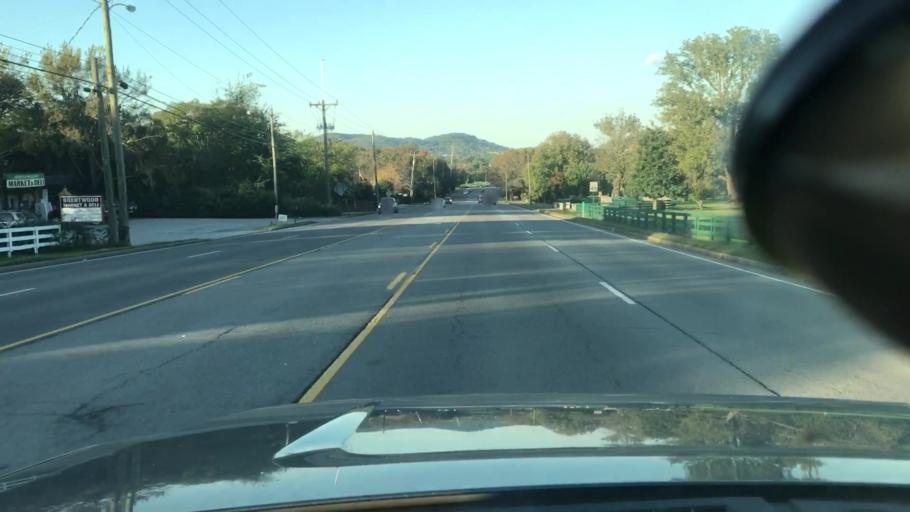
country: US
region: Tennessee
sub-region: Williamson County
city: Brentwood Estates
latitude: 36.0023
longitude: -86.8076
